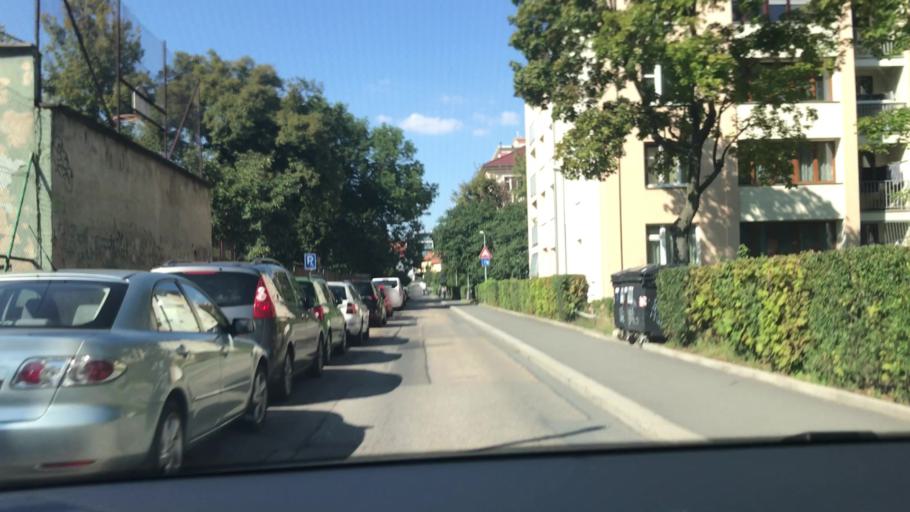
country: CZ
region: Praha
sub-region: Praha 8
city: Liben
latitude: 50.0742
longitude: 14.4937
